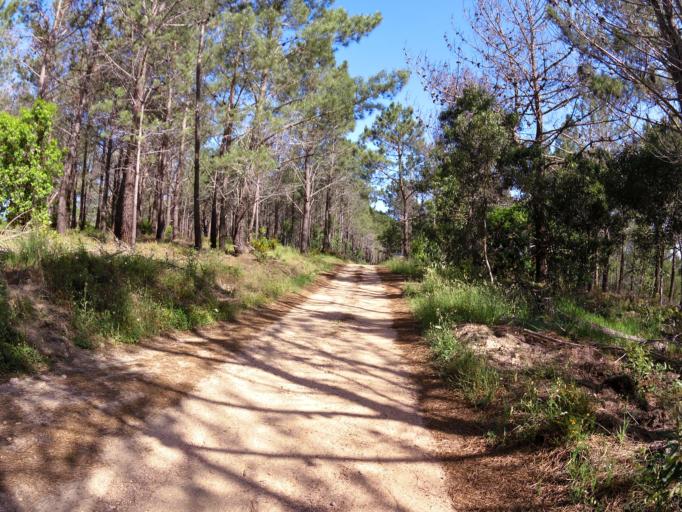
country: PT
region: Faro
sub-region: Aljezur
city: Aljezur
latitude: 37.3319
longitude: -8.8077
